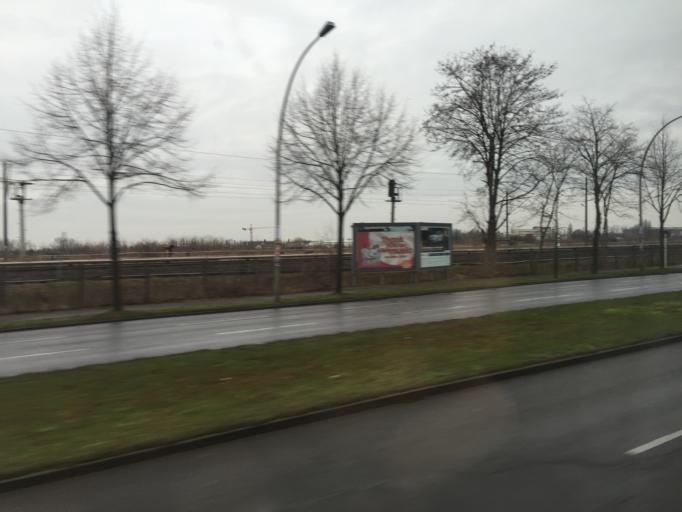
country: DE
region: Berlin
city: Adlershof
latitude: 52.4419
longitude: 13.5320
